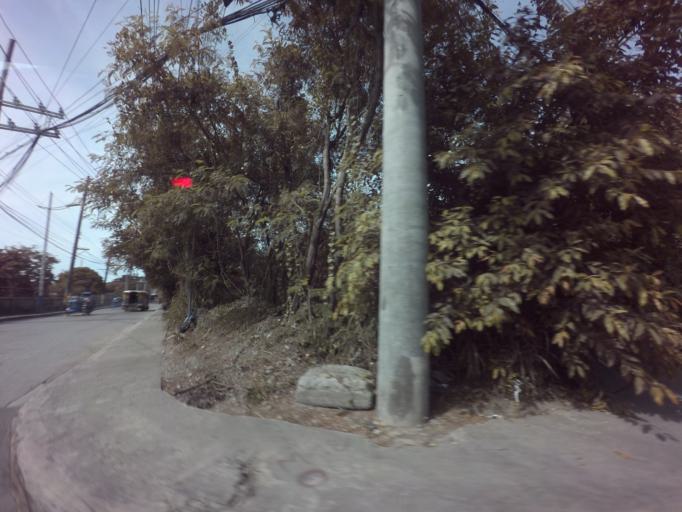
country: PH
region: Calabarzon
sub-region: Province of Rizal
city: Pateros
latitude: 14.5453
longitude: 121.0887
